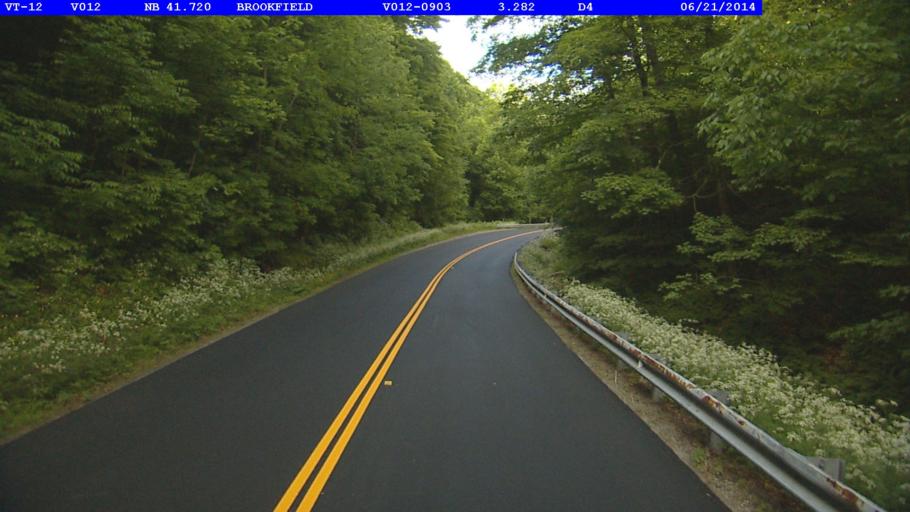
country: US
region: Vermont
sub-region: Washington County
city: Northfield
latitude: 44.0497
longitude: -72.6435
